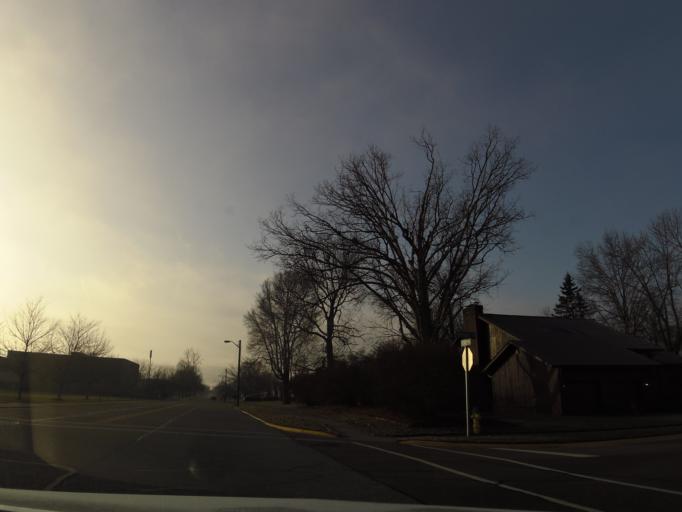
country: US
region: Indiana
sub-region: Bartholomew County
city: Columbus
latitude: 39.2291
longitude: -85.9124
